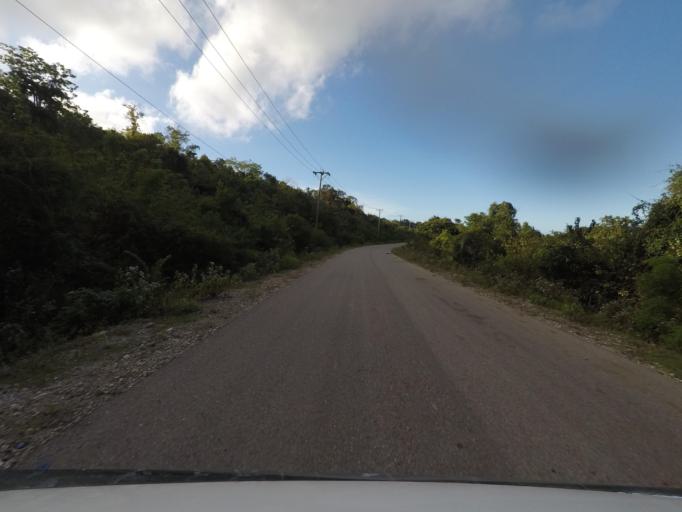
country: TL
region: Lautem
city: Lospalos
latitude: -8.4079
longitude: 126.9998
